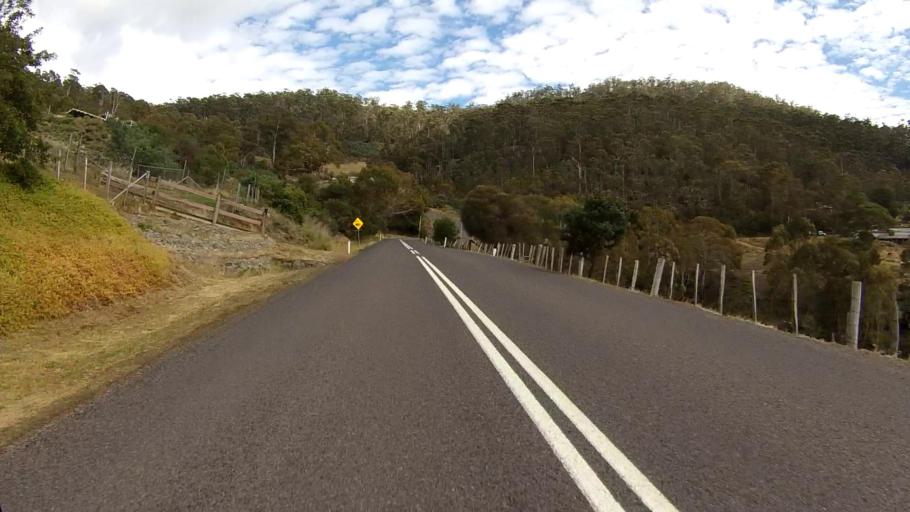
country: AU
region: Tasmania
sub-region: Clarence
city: Lindisfarne
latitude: -42.7850
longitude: 147.3589
